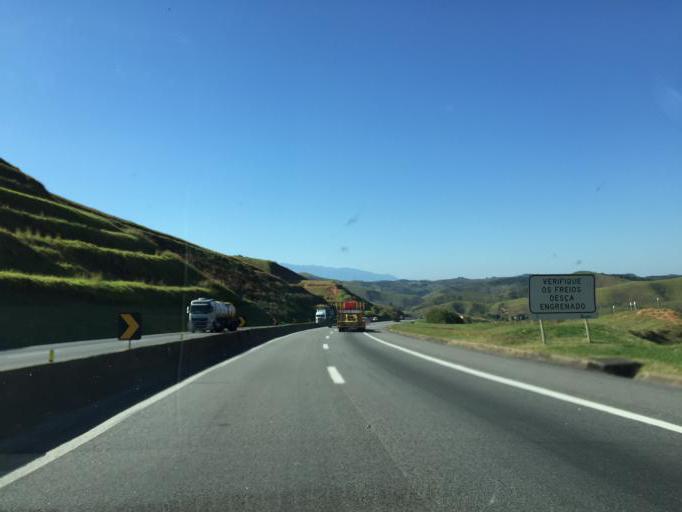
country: BR
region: Sao Paulo
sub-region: Cruzeiro
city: Cruzeiro
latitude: -22.6359
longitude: -44.9355
